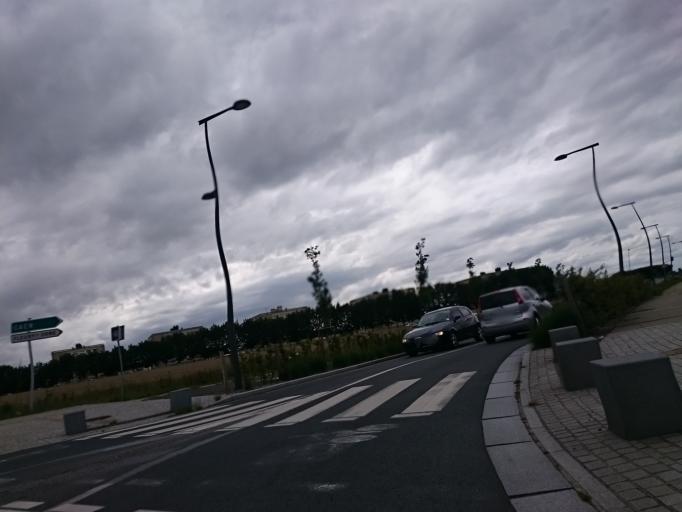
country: FR
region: Lower Normandy
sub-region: Departement du Calvados
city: Fleury-sur-Orne
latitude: 49.1442
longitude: -0.3721
